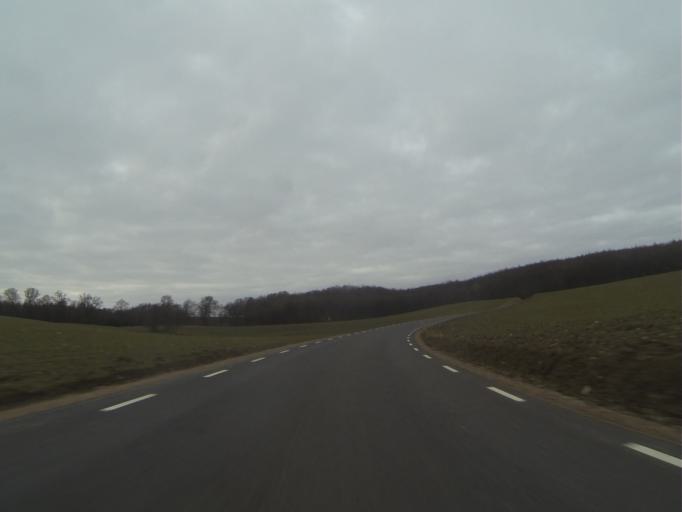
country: SE
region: Skane
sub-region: Lunds Kommun
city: Genarp
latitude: 55.5678
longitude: 13.4321
